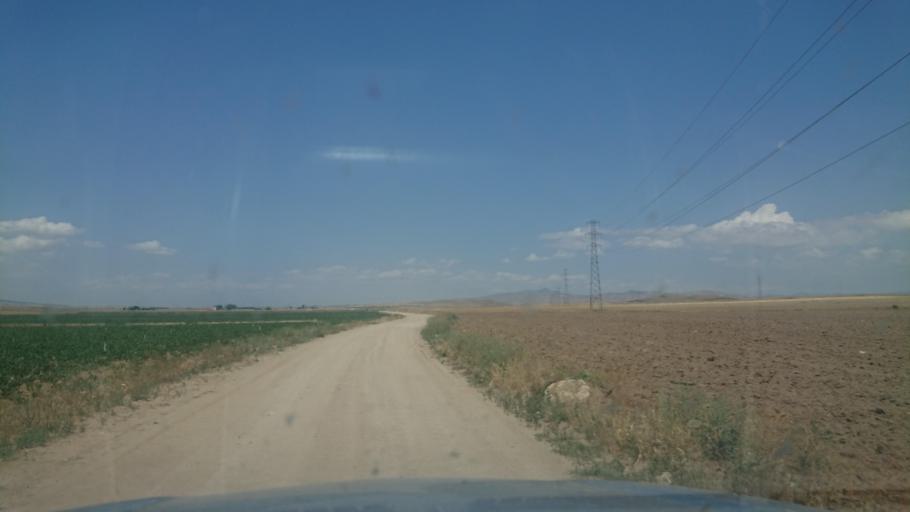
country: TR
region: Aksaray
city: Sariyahsi
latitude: 39.0110
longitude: 33.8798
